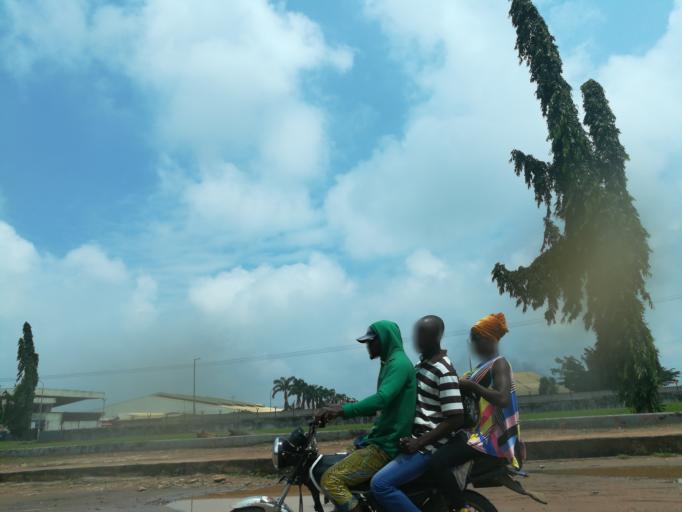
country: NG
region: Lagos
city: Ikorodu
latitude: 6.6740
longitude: 3.5126
